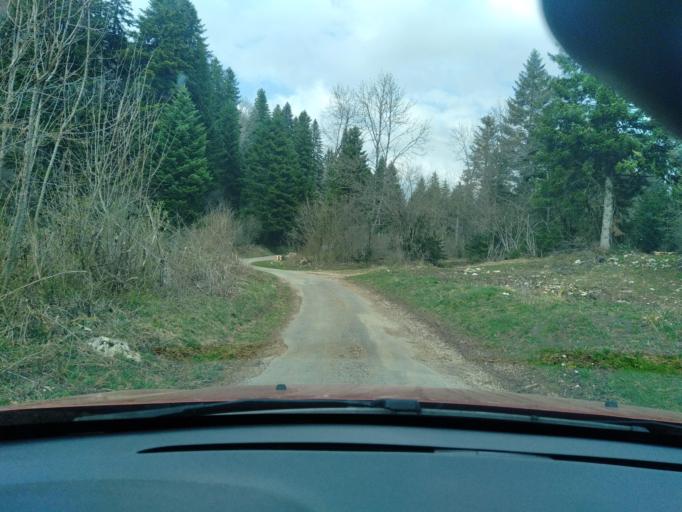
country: FR
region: Franche-Comte
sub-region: Departement du Jura
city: Moirans-en-Montagne
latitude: 46.4654
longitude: 5.7489
